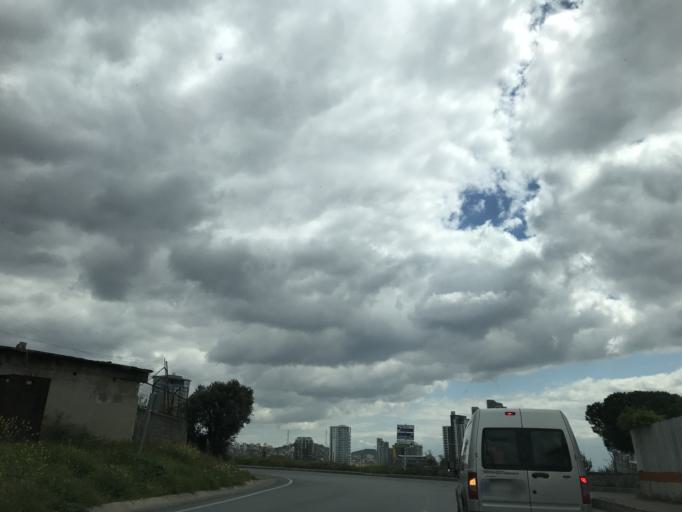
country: TR
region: Istanbul
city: Maltepe
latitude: 40.9036
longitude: 29.2098
